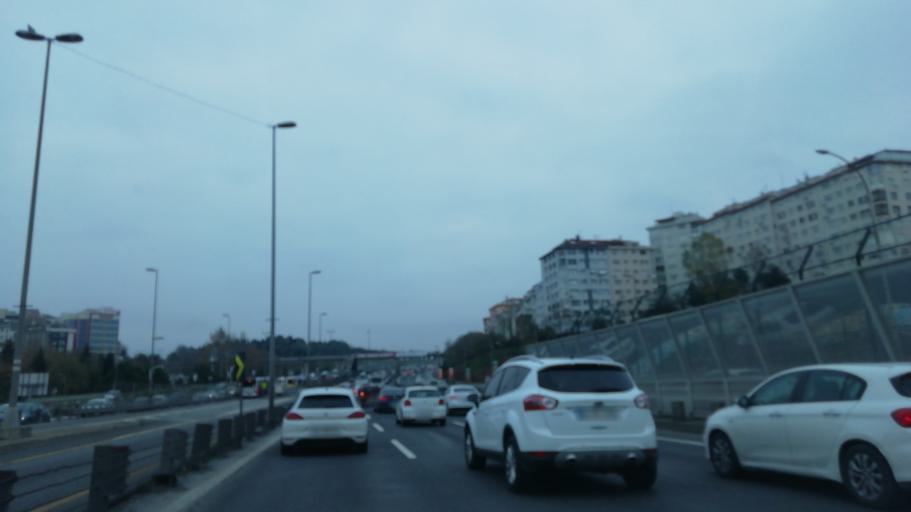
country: TR
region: Istanbul
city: Istanbul
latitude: 41.0472
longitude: 28.9449
